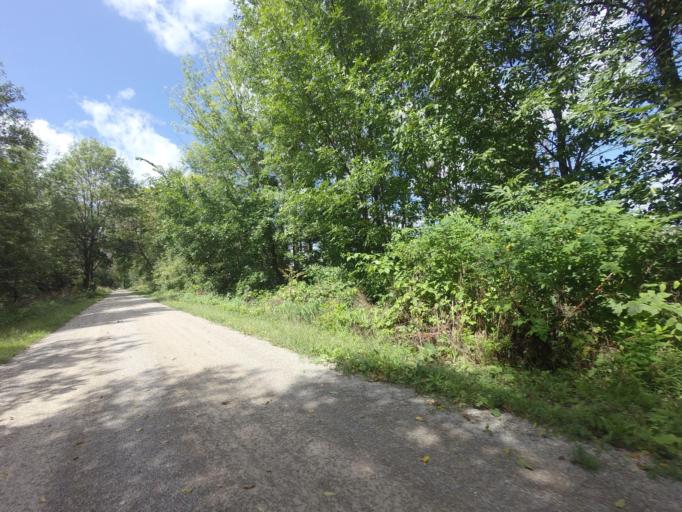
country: CA
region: Ontario
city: Huron East
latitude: 43.6118
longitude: -81.1338
